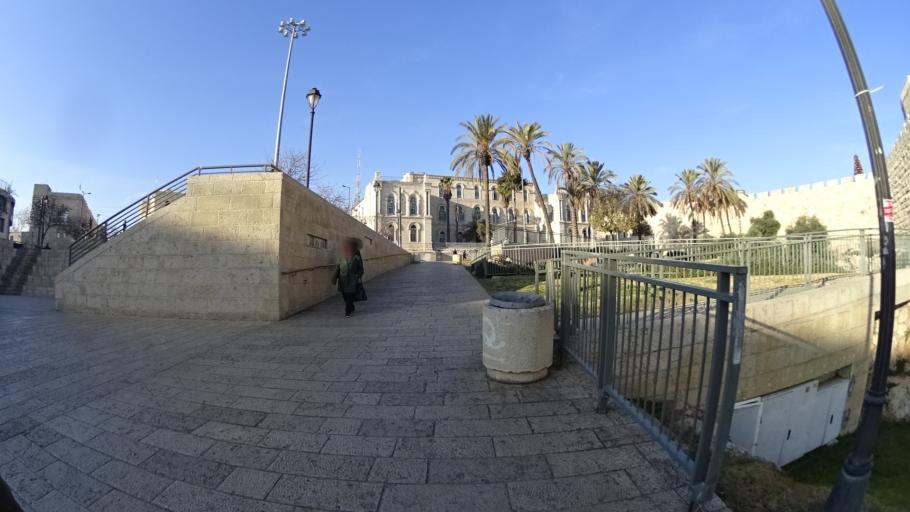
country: IL
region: Jerusalem
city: West Jerusalem
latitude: 31.7784
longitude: 35.2256
